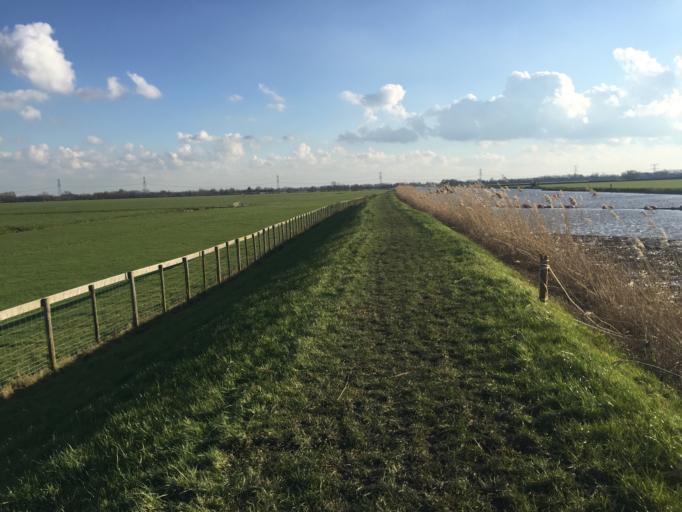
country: NL
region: South Holland
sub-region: Gemeente Vlist
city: Haastrecht
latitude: 52.0396
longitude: 4.8036
